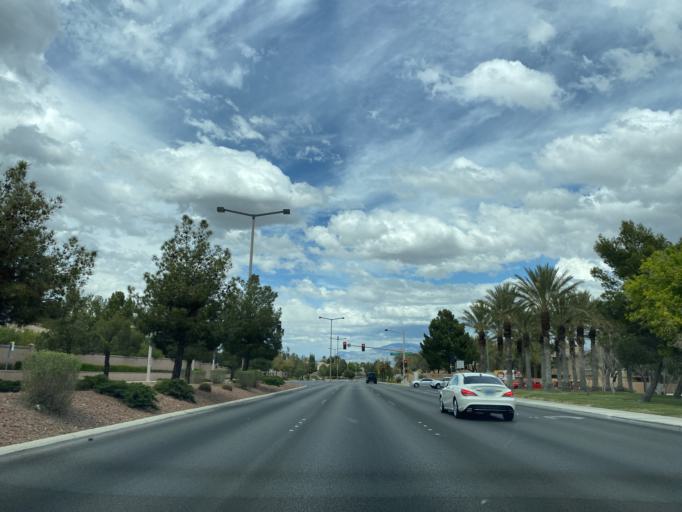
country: US
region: Nevada
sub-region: Clark County
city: Summerlin South
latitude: 36.1878
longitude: -115.2875
